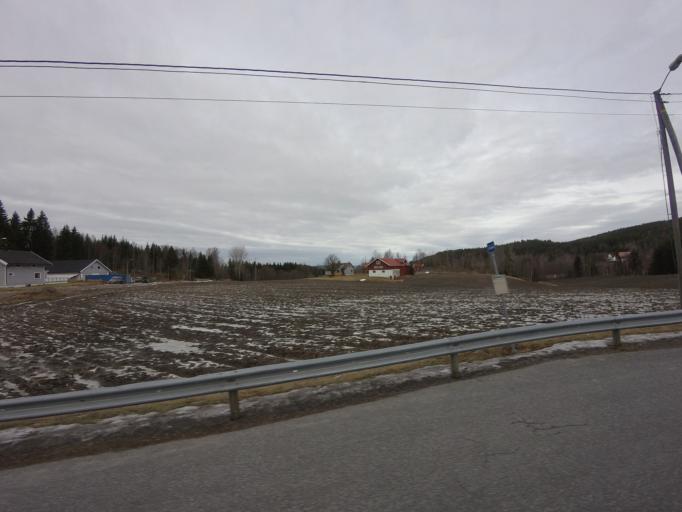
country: NO
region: Ostfold
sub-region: Trogstad
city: Skjonhaug
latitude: 59.7581
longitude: 11.2918
